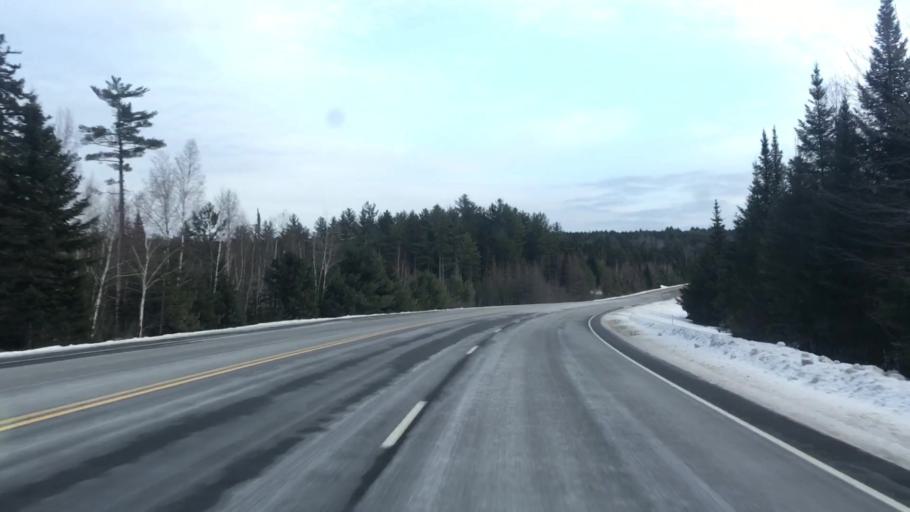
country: US
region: Maine
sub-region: Washington County
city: Addison
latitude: 44.9163
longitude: -67.7885
